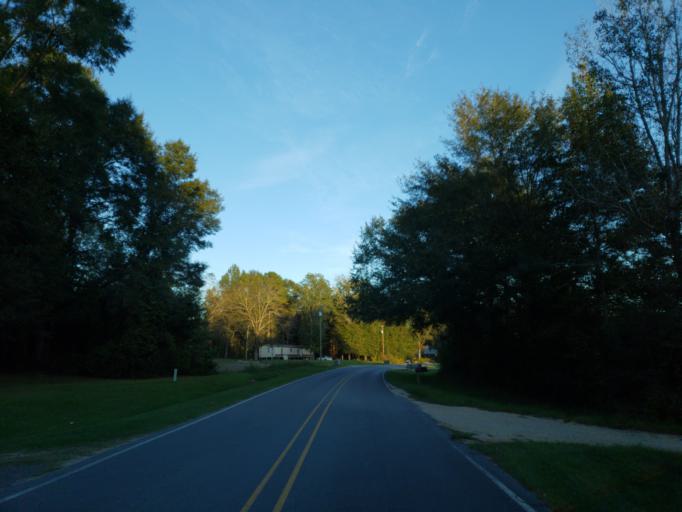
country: US
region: Mississippi
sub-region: Wayne County
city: Belmont
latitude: 31.4411
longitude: -88.5033
